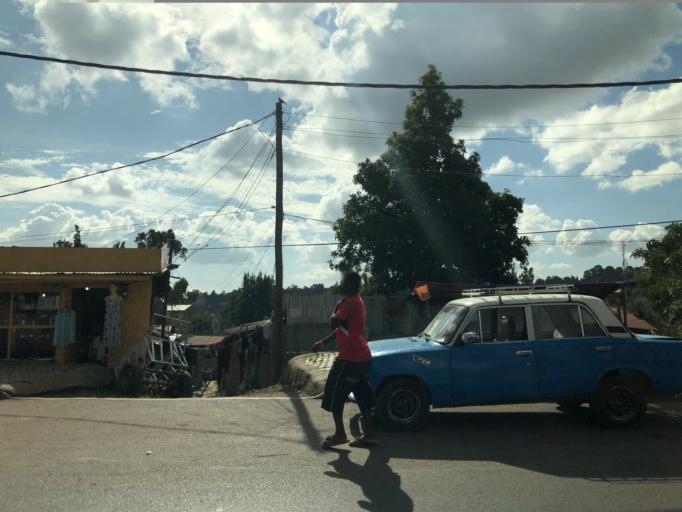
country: ET
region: Adis Abeba
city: Addis Ababa
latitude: 9.0297
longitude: 38.7742
